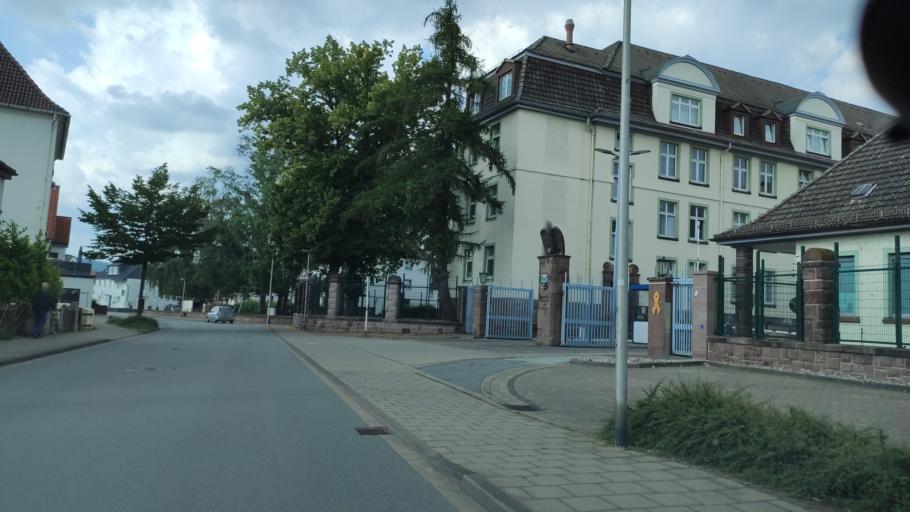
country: DE
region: Lower Saxony
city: Holzminden
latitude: 51.8322
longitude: 9.4602
